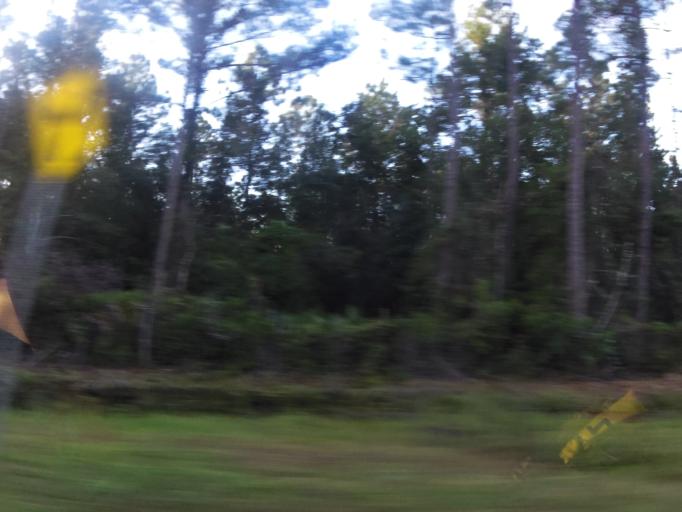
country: US
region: Georgia
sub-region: Camden County
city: Kings Bay Base
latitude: 30.7909
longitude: -81.5896
